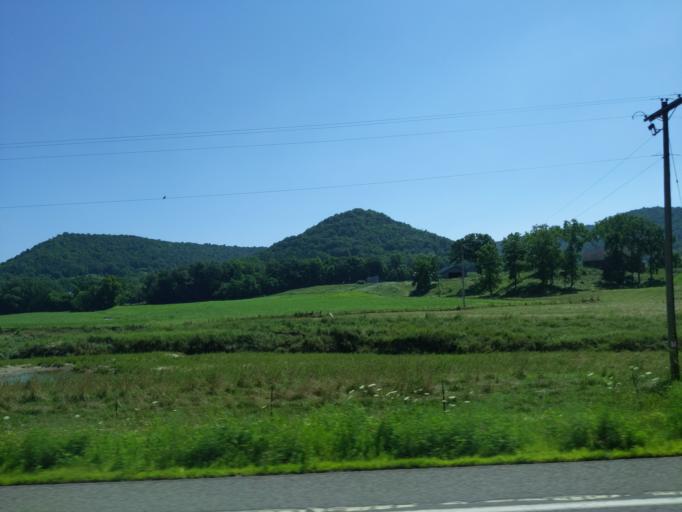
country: US
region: Wisconsin
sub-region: Vernon County
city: Westby
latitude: 43.6889
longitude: -91.0449
